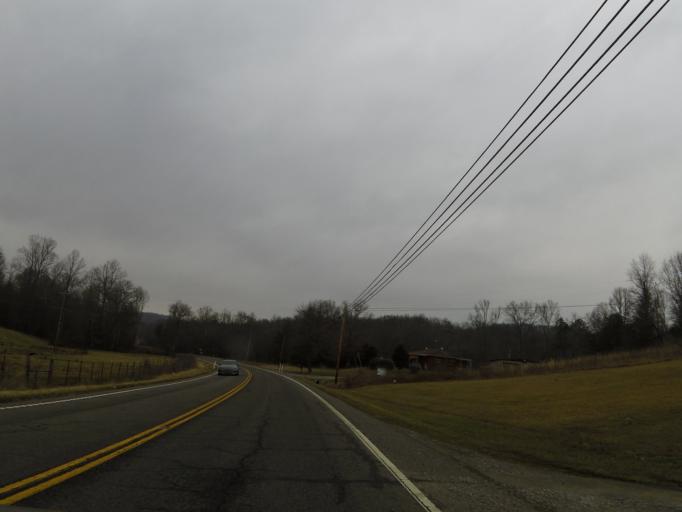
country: US
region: Tennessee
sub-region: Morgan County
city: Wartburg
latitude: 36.1770
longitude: -84.6558
